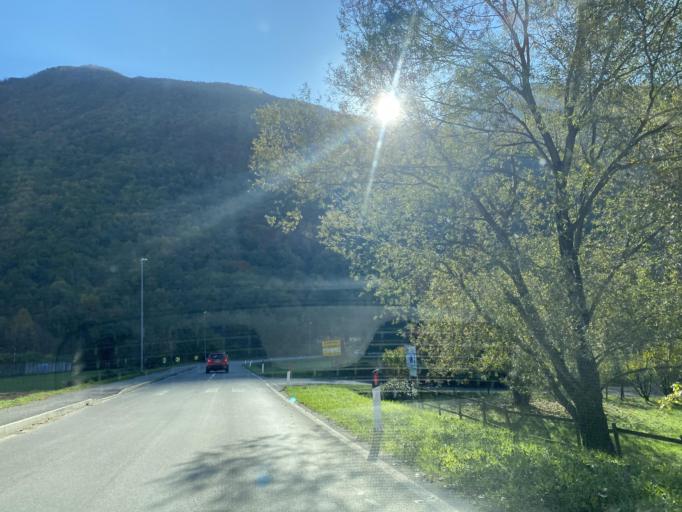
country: IT
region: Lombardy
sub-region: Provincia di Como
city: Porlezza
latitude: 46.0292
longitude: 9.1312
